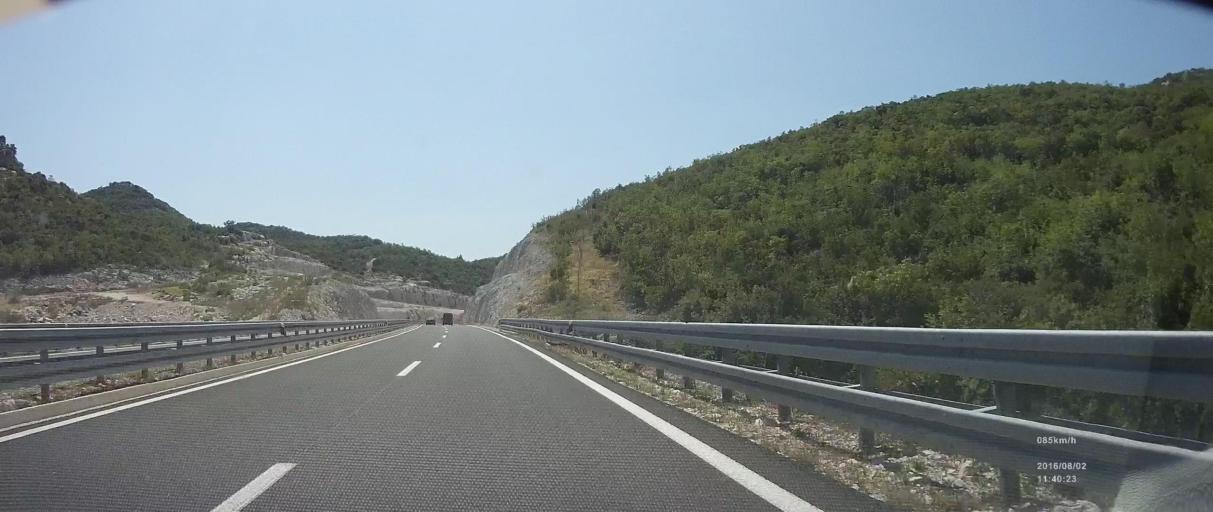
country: HR
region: Dubrovacko-Neretvanska
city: Komin
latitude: 43.0752
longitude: 17.4910
